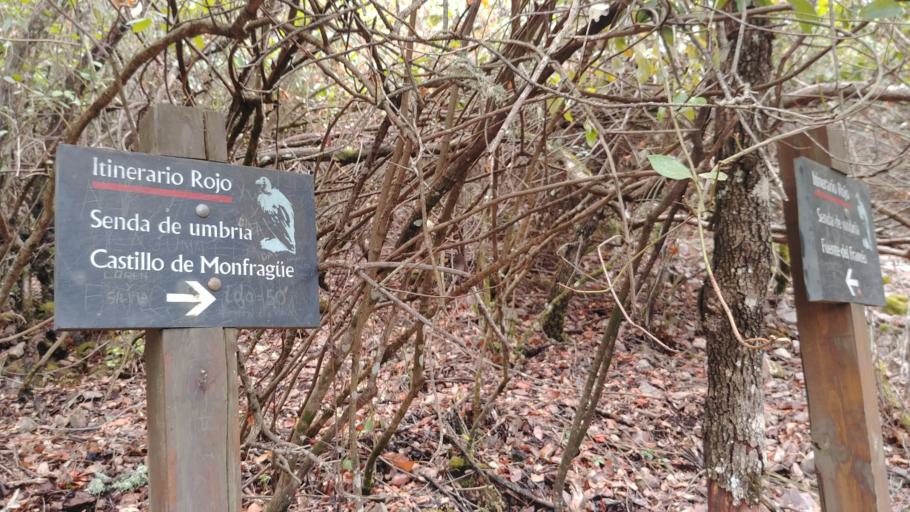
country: ES
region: Extremadura
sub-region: Provincia de Caceres
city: Torrejon el Rubio
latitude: 39.8295
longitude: -6.0359
